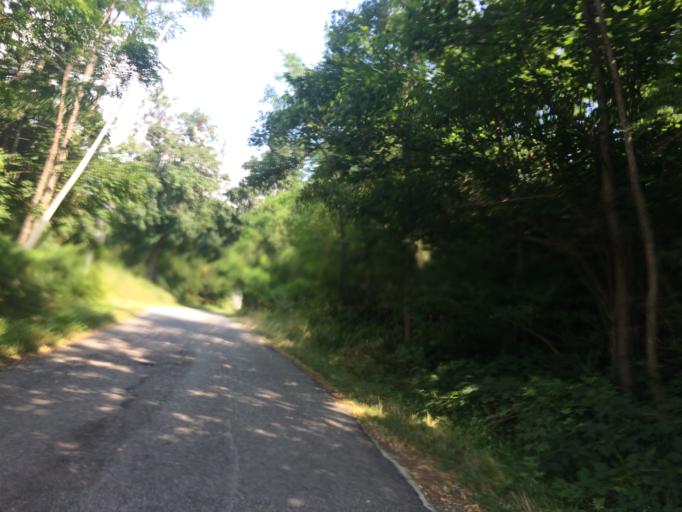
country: IT
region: Liguria
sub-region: Provincia di Savona
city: Molino-Pera
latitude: 44.4748
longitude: 8.3521
